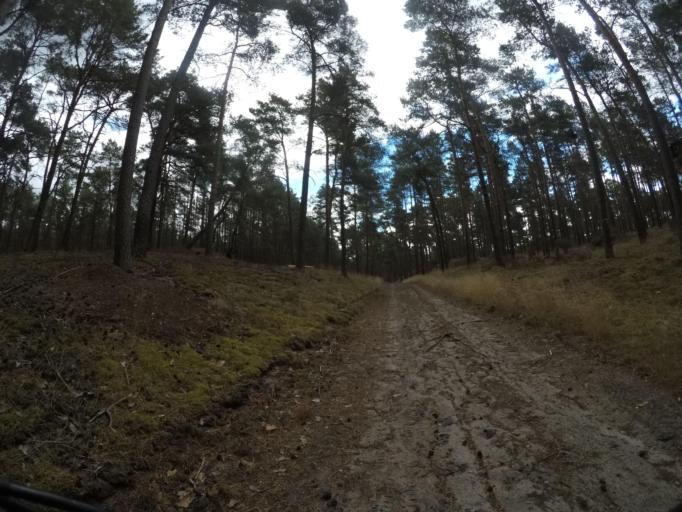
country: DE
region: Lower Saxony
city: Hitzacker
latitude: 53.1941
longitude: 11.0556
